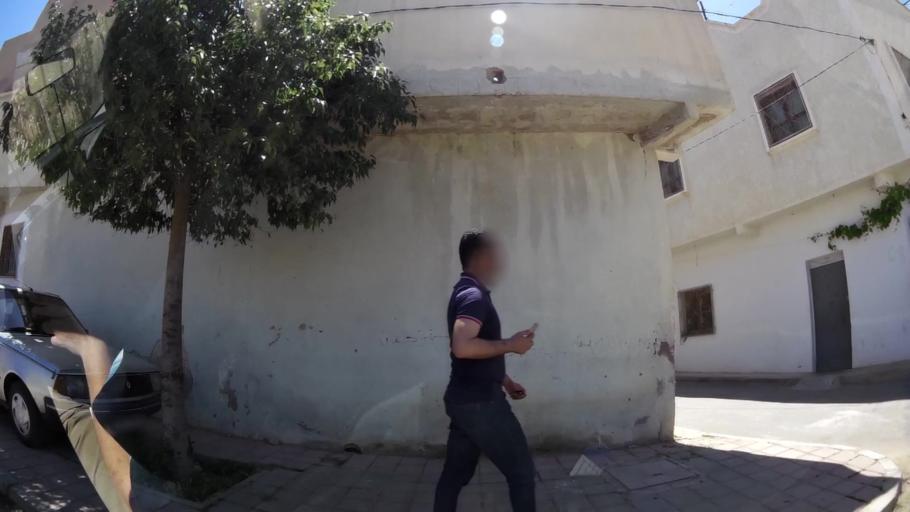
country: MA
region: Oriental
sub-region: Oujda-Angad
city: Oujda
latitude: 34.6944
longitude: -1.9458
